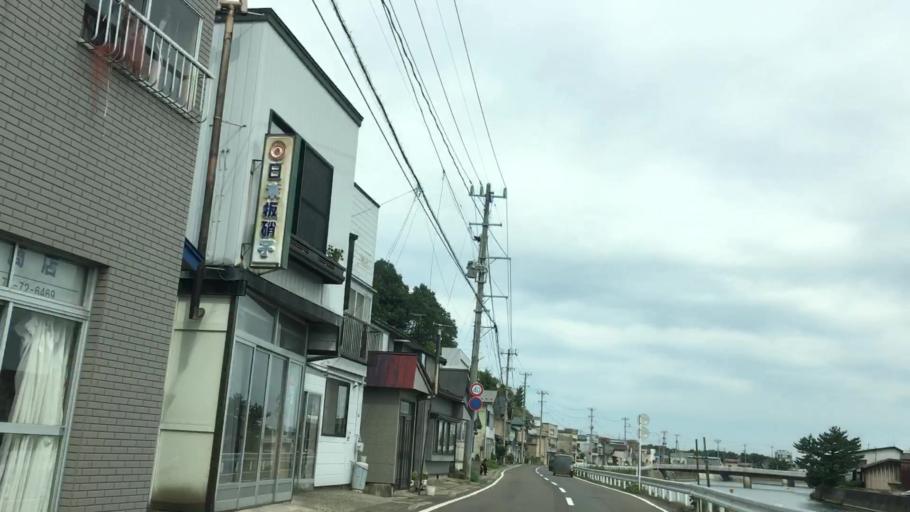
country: JP
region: Aomori
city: Shimokizukuri
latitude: 40.7747
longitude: 140.2161
